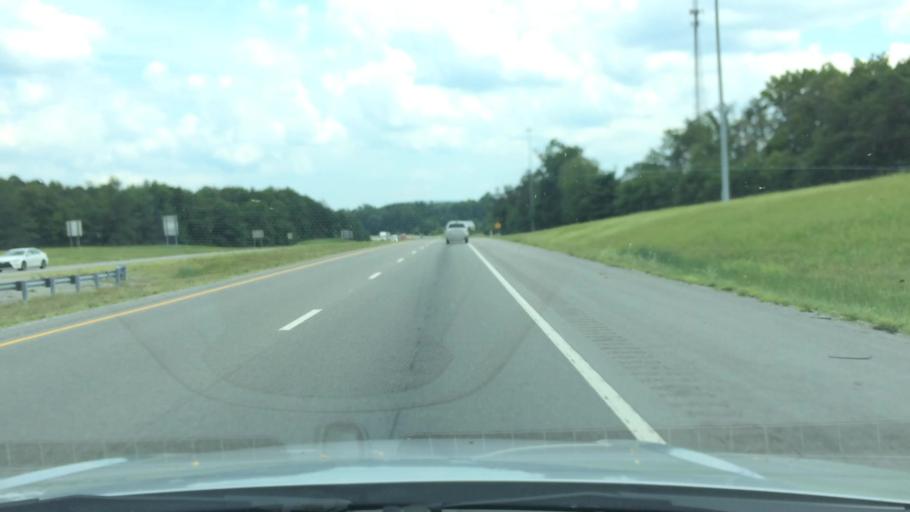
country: US
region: Tennessee
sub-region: Cumberland County
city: Crossville
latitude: 35.9622
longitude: -84.9827
